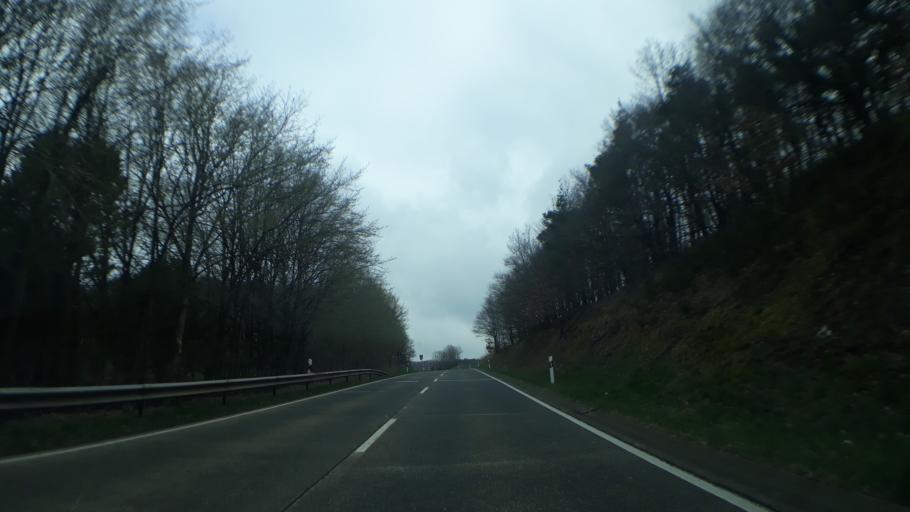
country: DE
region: North Rhine-Westphalia
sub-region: Regierungsbezirk Koln
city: Schleiden
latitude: 50.5478
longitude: 6.4712
